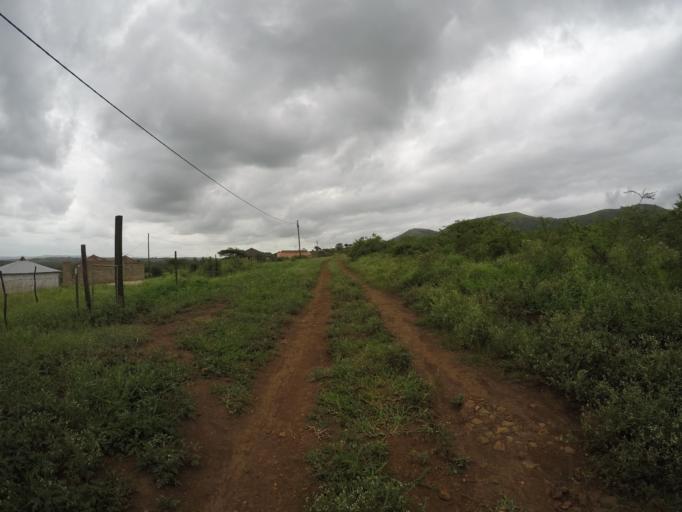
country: ZA
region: KwaZulu-Natal
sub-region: uThungulu District Municipality
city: Empangeni
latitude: -28.5885
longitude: 31.8615
